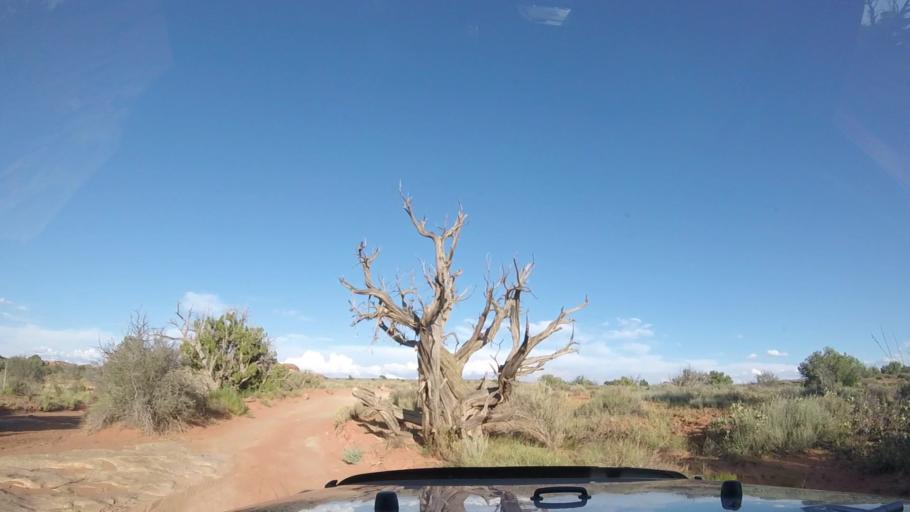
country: US
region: Utah
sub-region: Grand County
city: Moab
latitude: 38.2081
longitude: -109.7870
